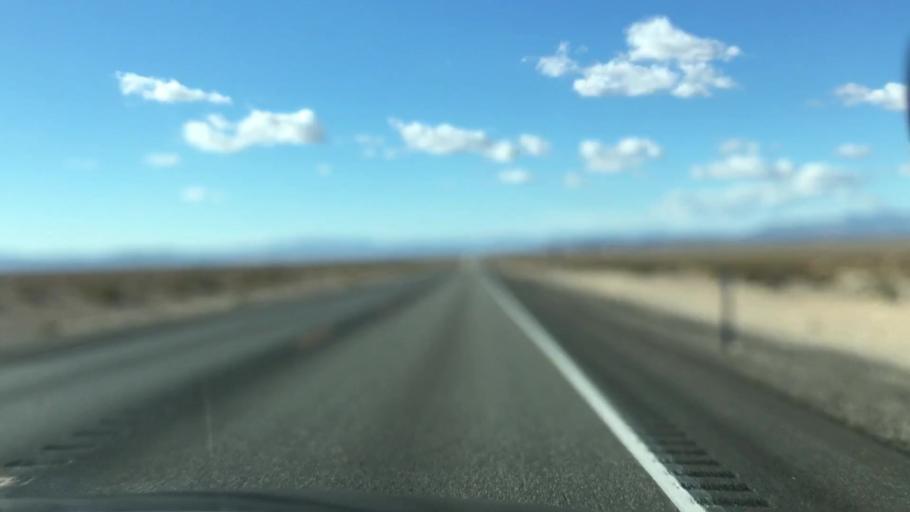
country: US
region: Nevada
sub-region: Nye County
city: Beatty
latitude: 36.6338
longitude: -116.3592
